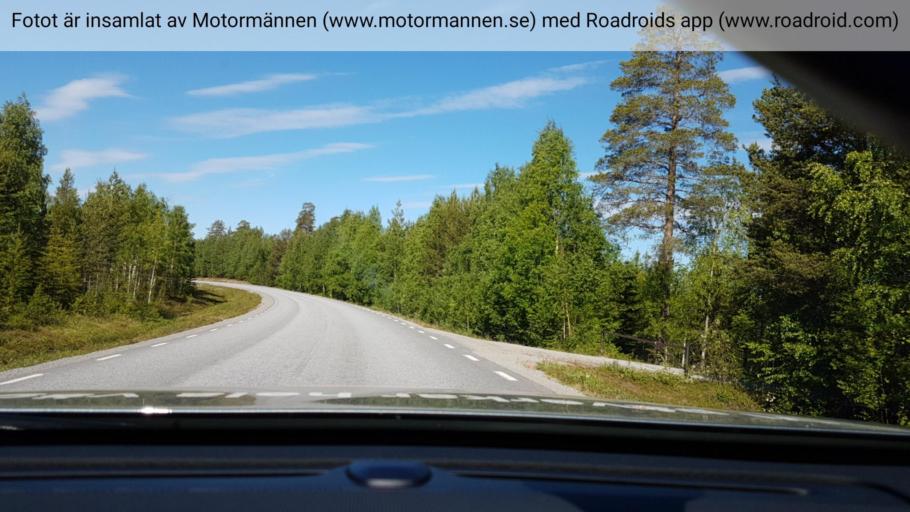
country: SE
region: Vaesterbotten
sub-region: Lycksele Kommun
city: Lycksele
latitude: 64.0620
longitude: 18.4914
